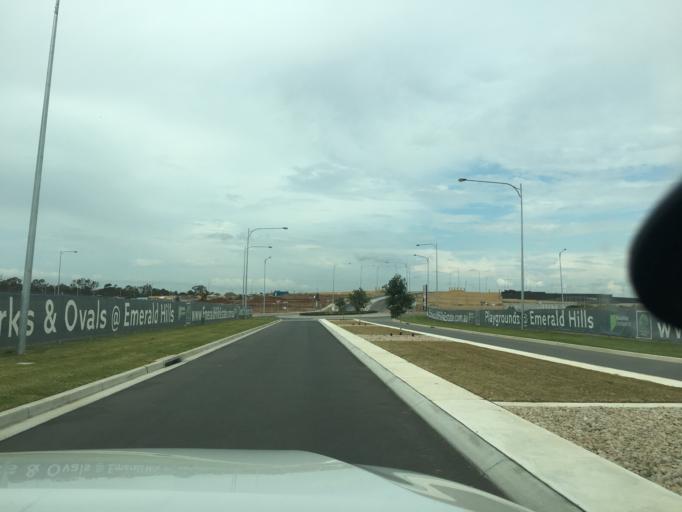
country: AU
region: New South Wales
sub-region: Campbelltown Municipality
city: Denham Court
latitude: -33.9867
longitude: 150.7966
